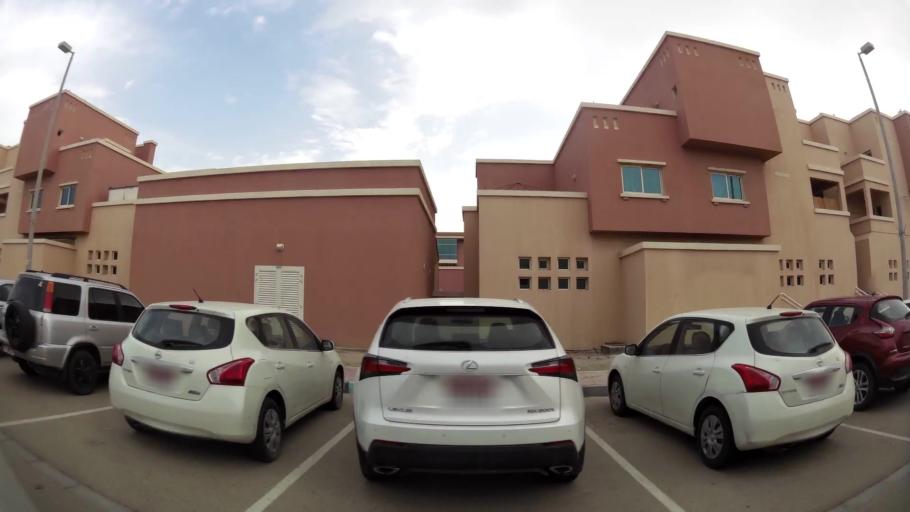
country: AE
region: Abu Dhabi
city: Abu Dhabi
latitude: 24.4757
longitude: 54.3845
